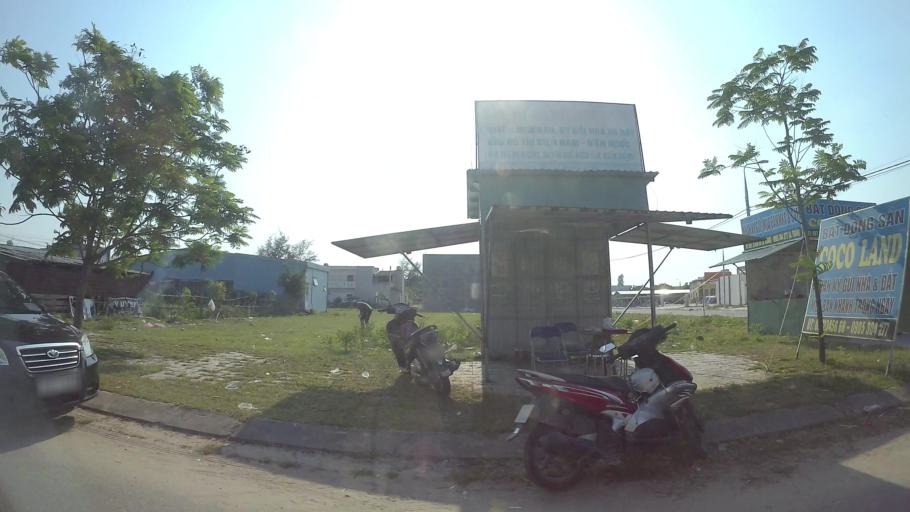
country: VN
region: Da Nang
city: Ngu Hanh Son
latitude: 15.9526
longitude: 108.2598
